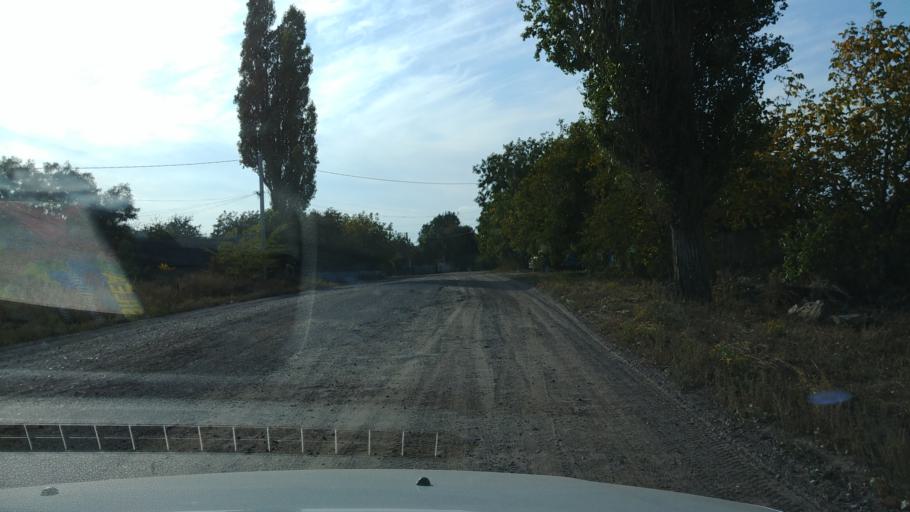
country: MD
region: Rezina
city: Rezina
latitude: 47.7452
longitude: 28.8923
